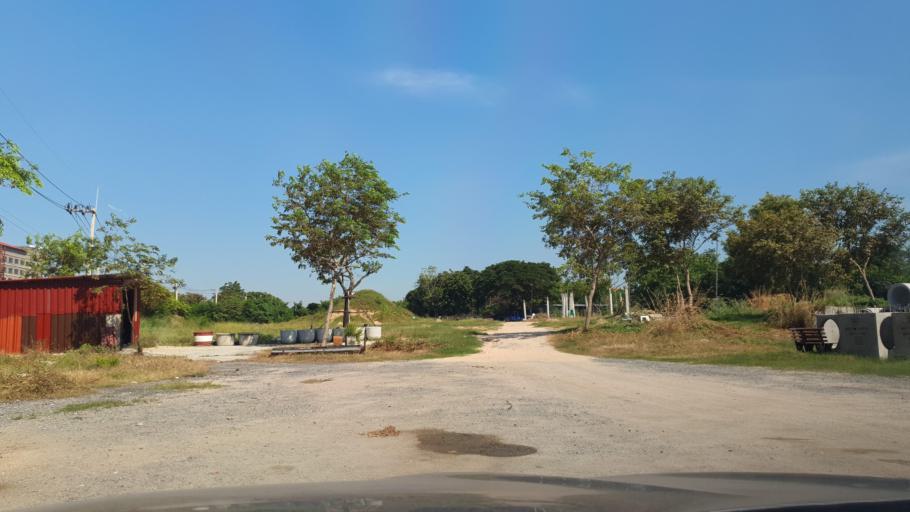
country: TH
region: Chon Buri
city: Phatthaya
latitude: 12.8629
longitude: 100.8970
